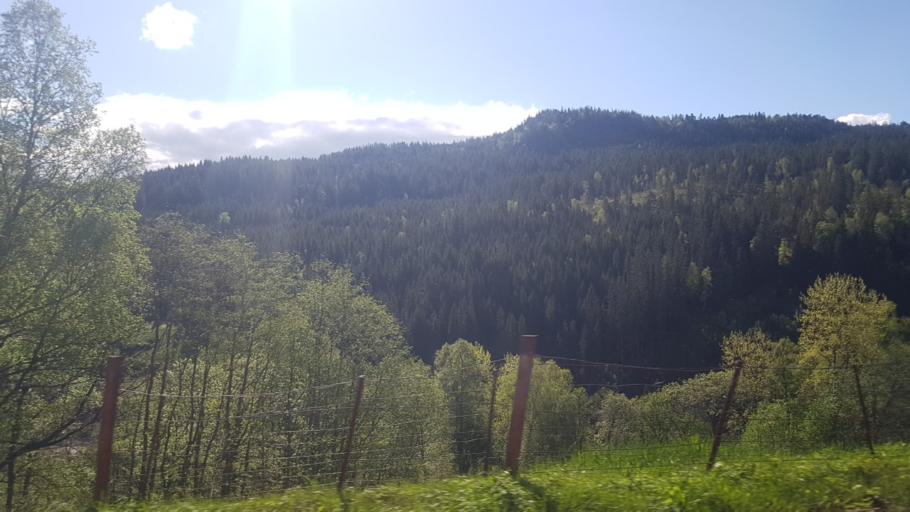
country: NO
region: Sor-Trondelag
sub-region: Midtre Gauldal
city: Storen
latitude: 62.9451
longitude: 10.1896
